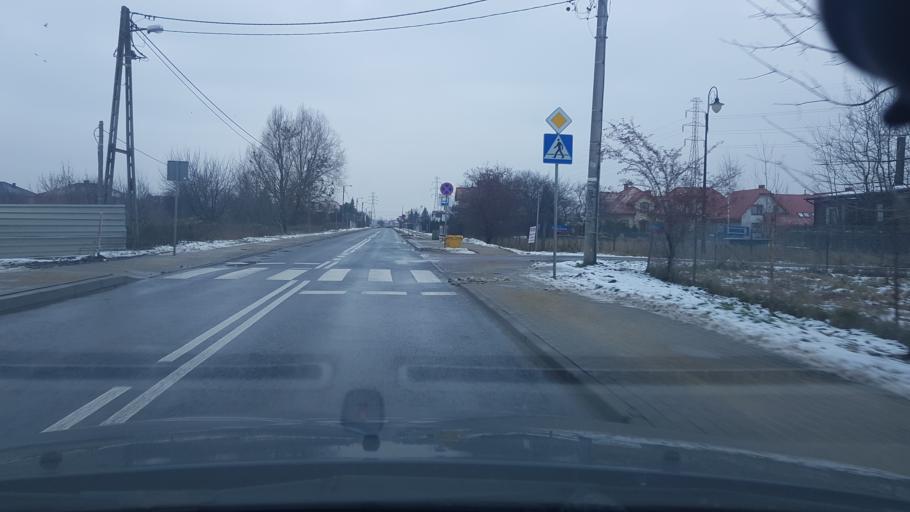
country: PL
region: Masovian Voivodeship
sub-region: Warszawa
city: Targowek
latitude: 52.3142
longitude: 21.0382
